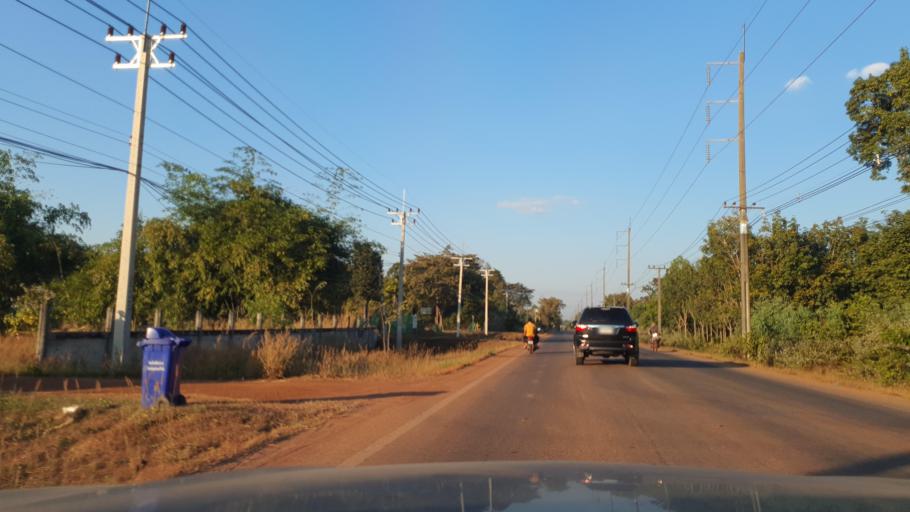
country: TH
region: Nakhon Phanom
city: Si Songkhram
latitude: 17.5965
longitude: 104.2375
